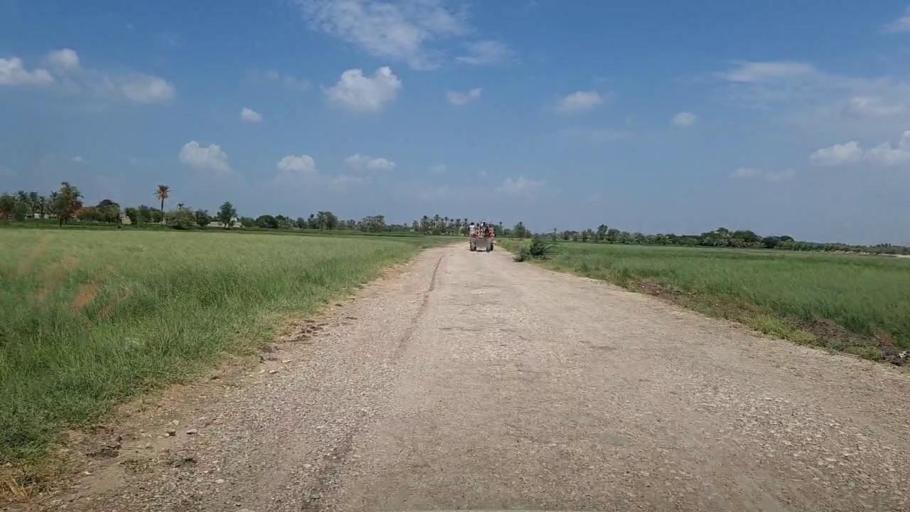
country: PK
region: Sindh
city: Bhiria
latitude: 26.9516
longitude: 68.2345
